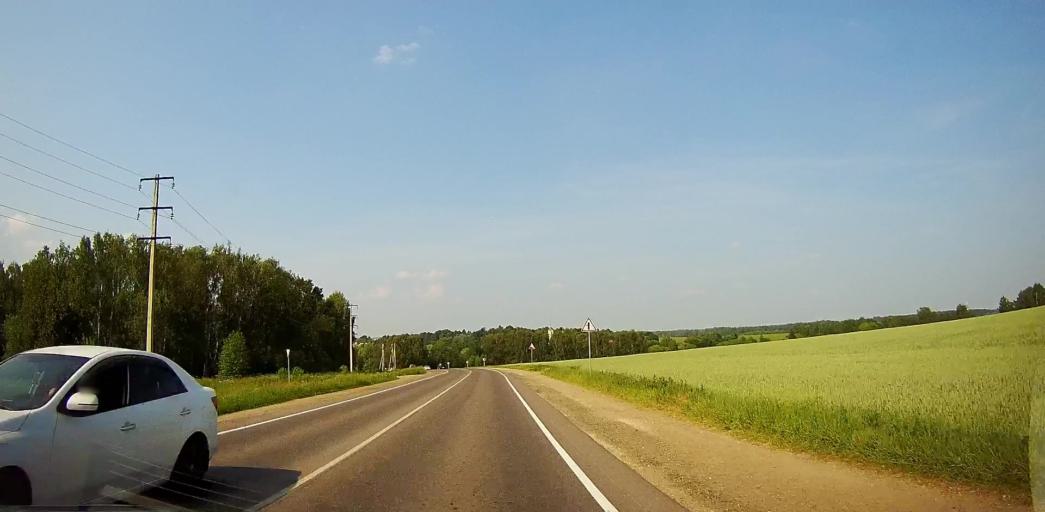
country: RU
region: Moskovskaya
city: Barybino
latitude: 55.2898
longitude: 37.9126
